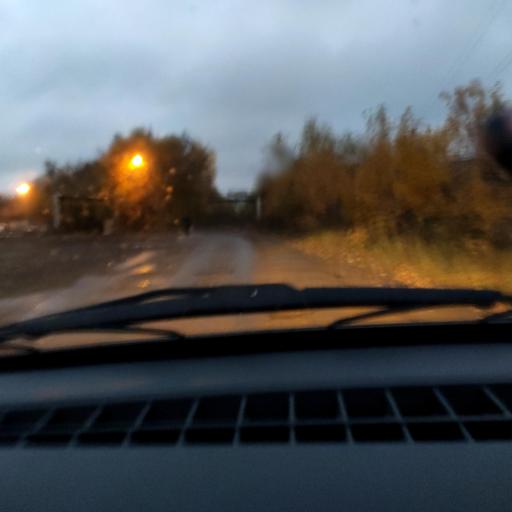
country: RU
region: Bashkortostan
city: Ufa
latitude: 54.7931
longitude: 56.0869
